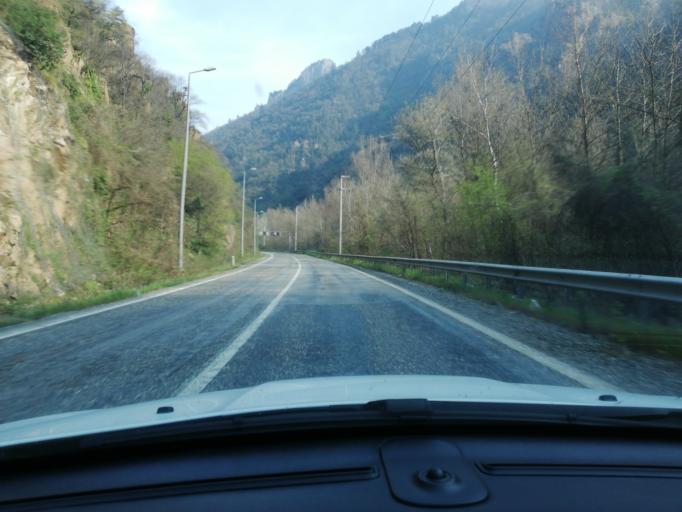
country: TR
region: Karabuk
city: Yenice
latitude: 41.1797
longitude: 32.4482
